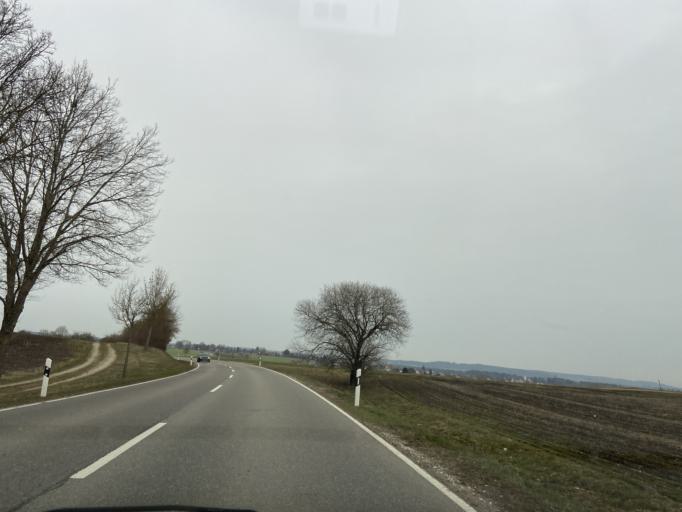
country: DE
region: Baden-Wuerttemberg
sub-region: Tuebingen Region
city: Ostrach
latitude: 47.9141
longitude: 9.3295
